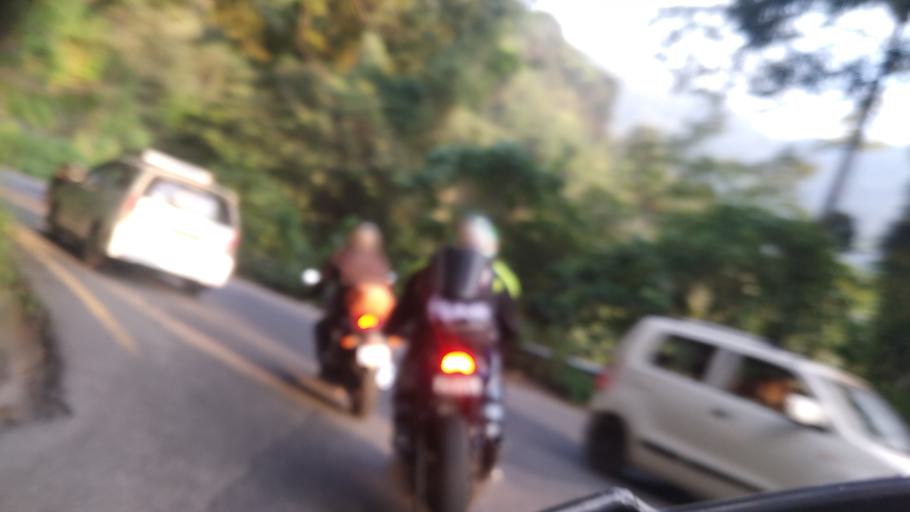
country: IN
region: Kerala
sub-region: Wayanad
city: Kalpetta
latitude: 11.5091
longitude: 76.0272
